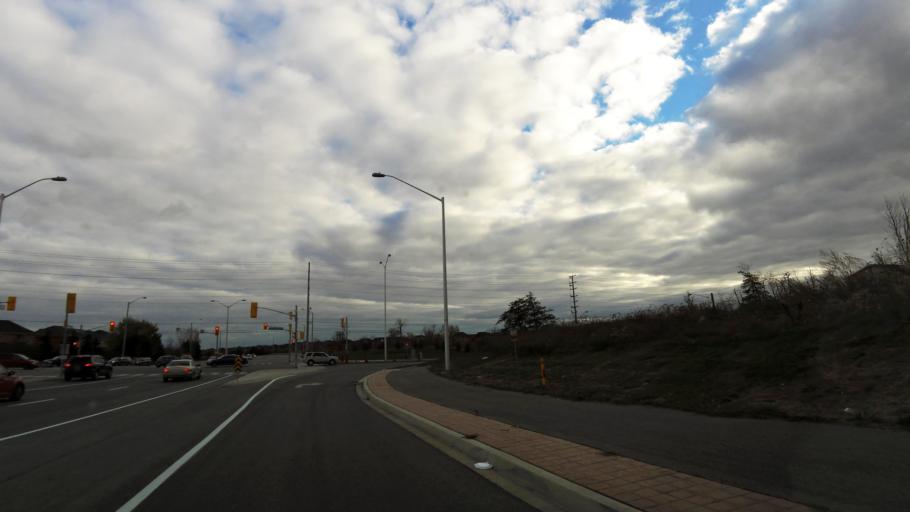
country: CA
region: Ontario
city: Brampton
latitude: 43.7670
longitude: -79.7191
